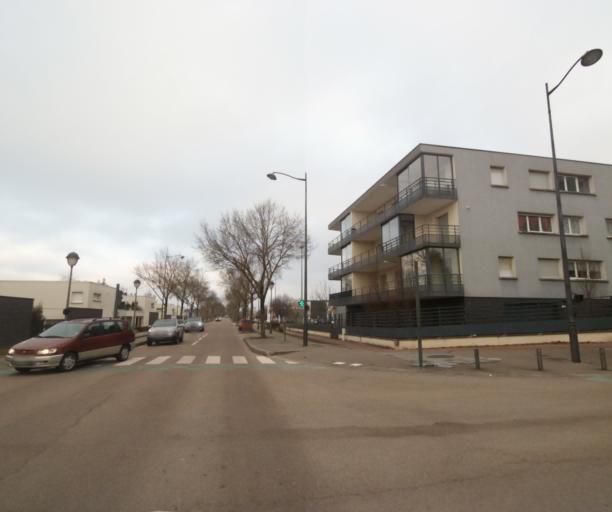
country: FR
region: Champagne-Ardenne
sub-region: Departement de la Haute-Marne
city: Bettancourt-la-Ferree
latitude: 48.6391
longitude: 4.9720
